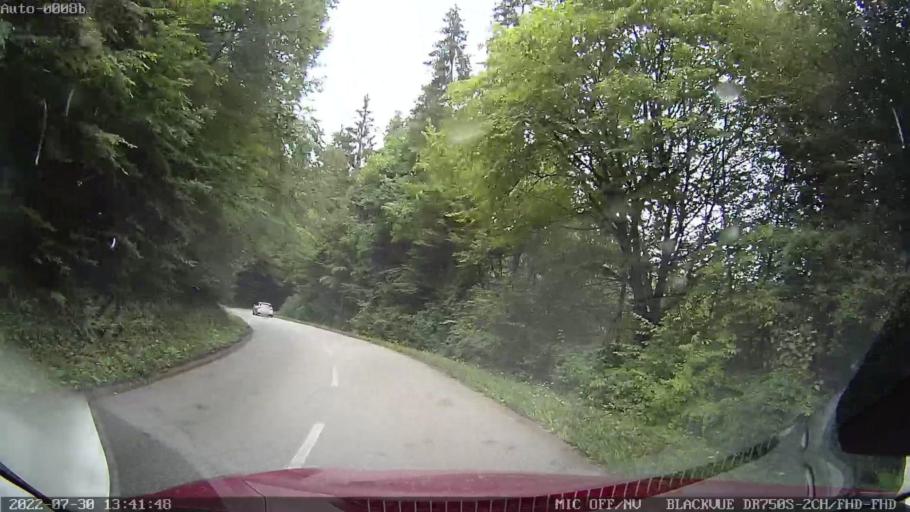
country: SI
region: Ivancna Gorica
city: Sentvid pri Sticni
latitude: 45.9030
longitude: 14.8952
